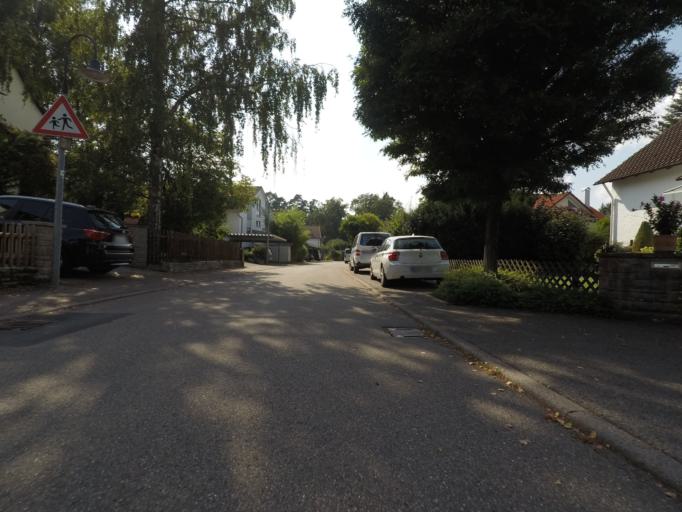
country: DE
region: Baden-Wuerttemberg
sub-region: Regierungsbezirk Stuttgart
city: Steinenbronn
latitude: 48.6556
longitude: 9.1138
